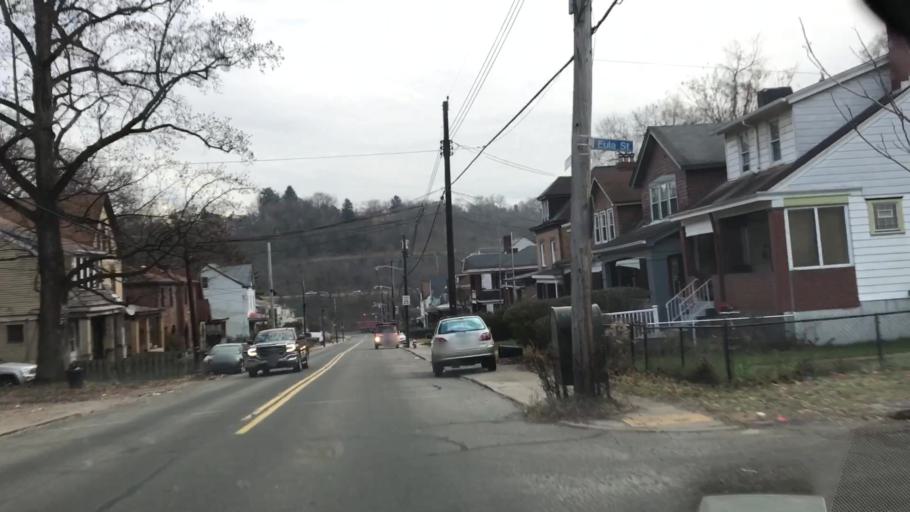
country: US
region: Pennsylvania
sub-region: Allegheny County
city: Millvale
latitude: 40.4887
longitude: -80.0135
